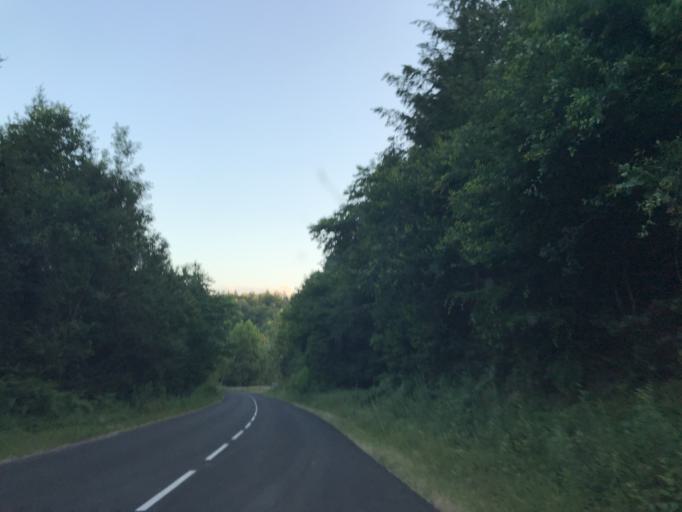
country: FR
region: Auvergne
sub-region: Departement du Puy-de-Dome
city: Courpiere
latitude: 45.7416
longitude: 3.6025
